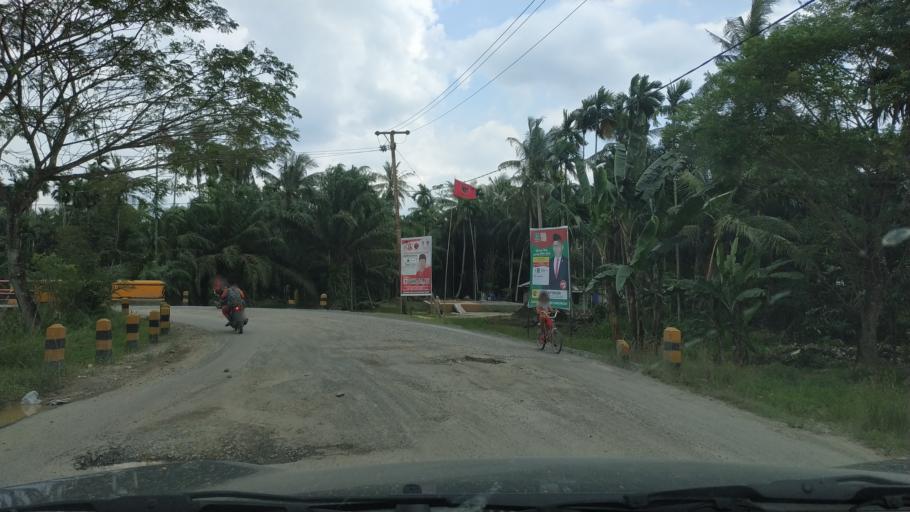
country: ID
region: Riau
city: Sungaisalak
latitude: -0.5678
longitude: 102.9686
